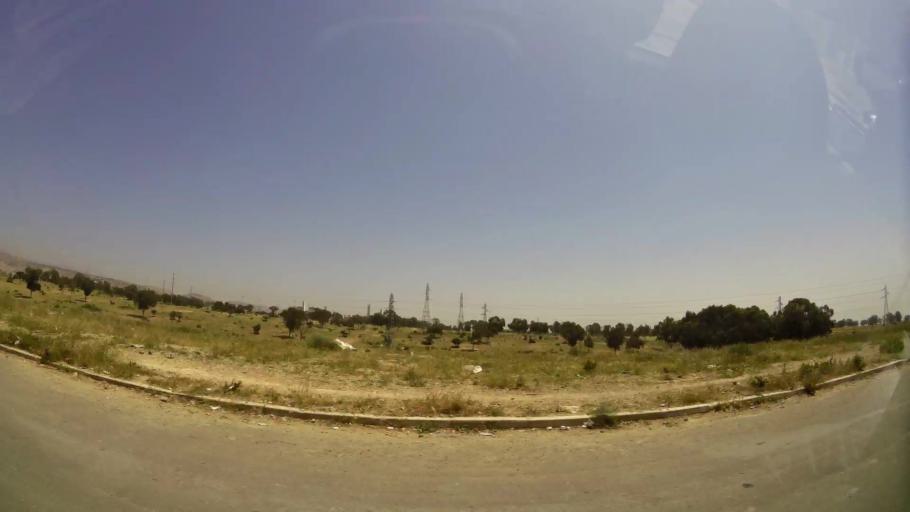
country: MA
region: Oued ed Dahab-Lagouira
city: Dakhla
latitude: 30.4264
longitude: -9.5524
